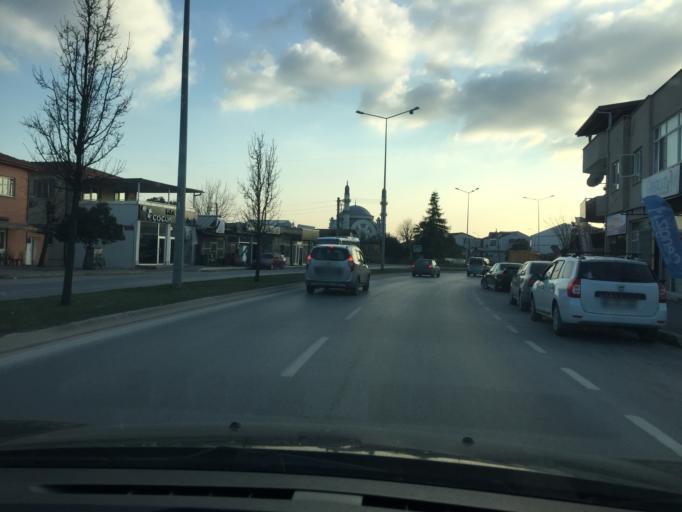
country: TR
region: Sakarya
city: Adapazari
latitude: 40.7907
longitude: 30.4074
